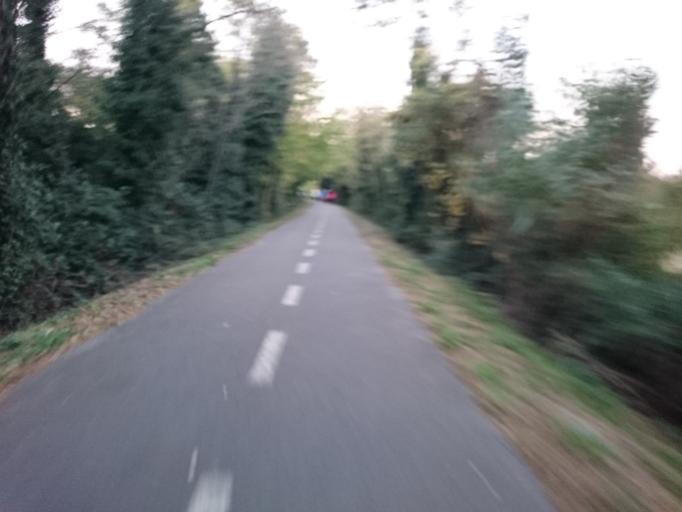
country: SI
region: Koper-Capodistria
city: Prade
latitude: 45.5500
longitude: 13.7856
